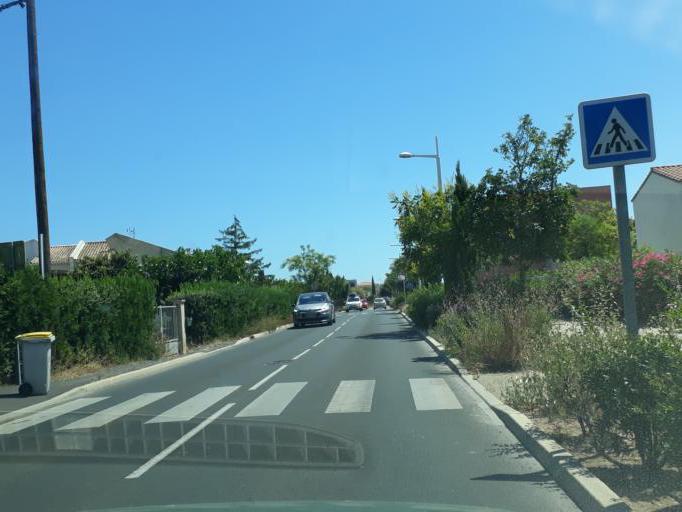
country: FR
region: Languedoc-Roussillon
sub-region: Departement de l'Herault
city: Agde
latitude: 43.3041
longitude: 3.4771
